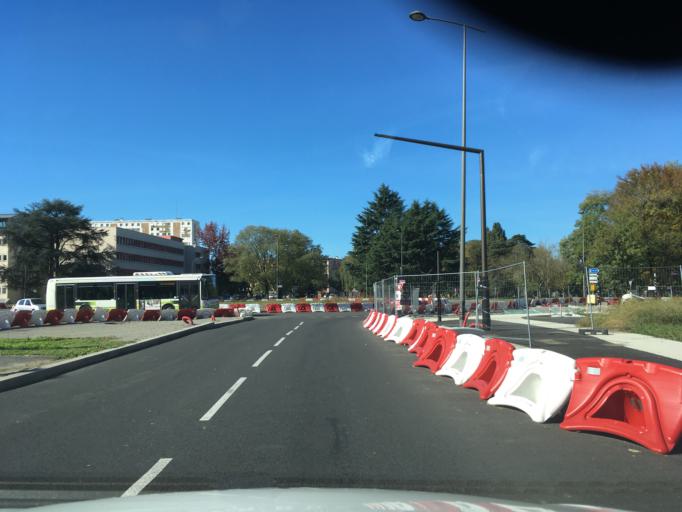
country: FR
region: Aquitaine
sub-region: Departement des Pyrenees-Atlantiques
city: Pau
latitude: 43.3113
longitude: -0.3620
